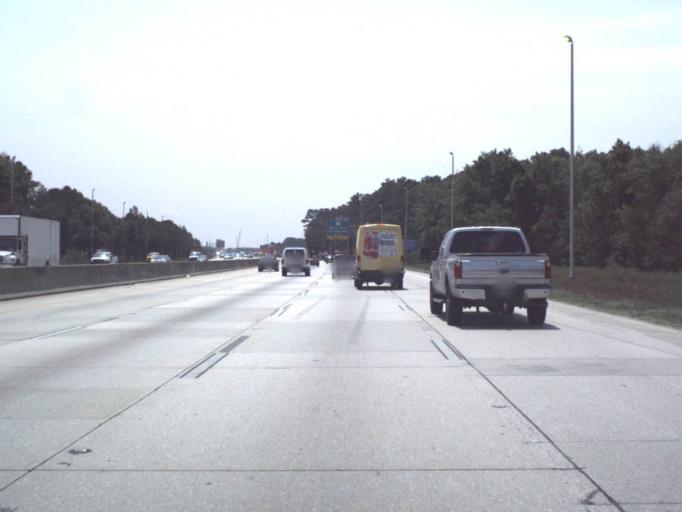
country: US
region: Florida
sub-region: Duval County
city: Jacksonville
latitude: 30.2613
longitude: -81.6065
